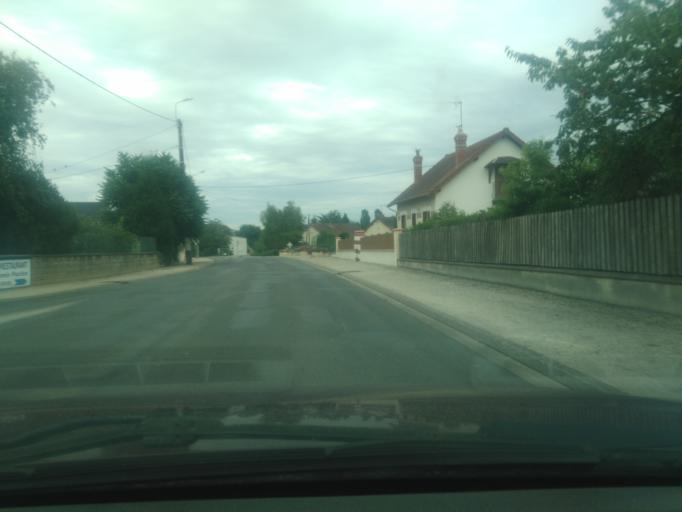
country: FR
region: Centre
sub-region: Departement du Cher
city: Orval
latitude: 46.7229
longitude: 2.4729
